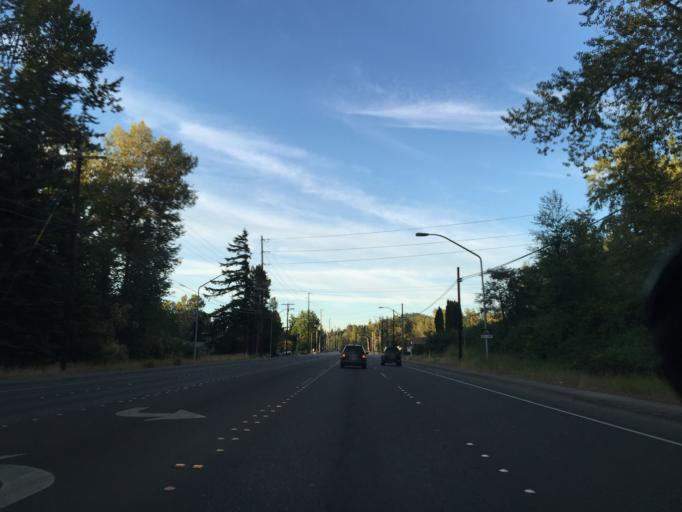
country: US
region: Washington
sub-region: Whatcom County
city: Geneva
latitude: 48.7788
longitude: -122.4381
